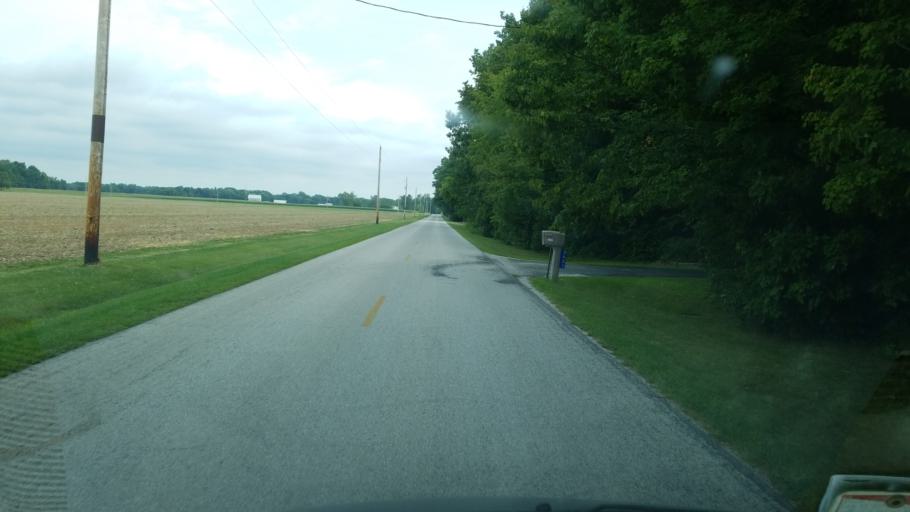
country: US
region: Ohio
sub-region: Sandusky County
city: Green Springs
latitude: 41.1771
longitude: -83.1030
